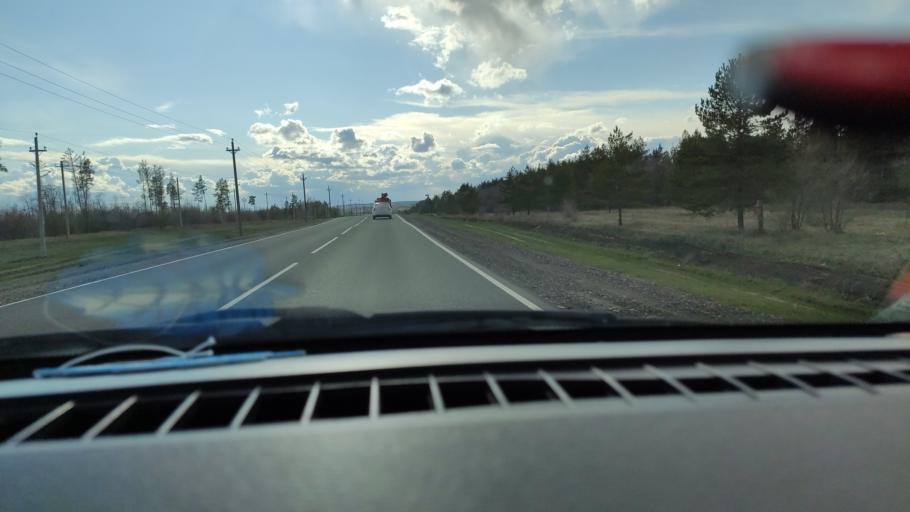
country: RU
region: Saratov
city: Sennoy
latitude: 52.1437
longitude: 46.9263
